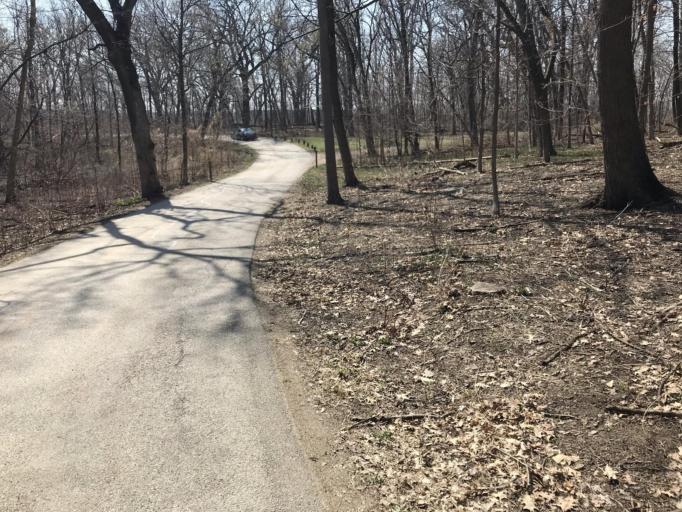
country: US
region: Illinois
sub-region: DuPage County
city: Downers Grove
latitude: 41.8132
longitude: -88.0396
